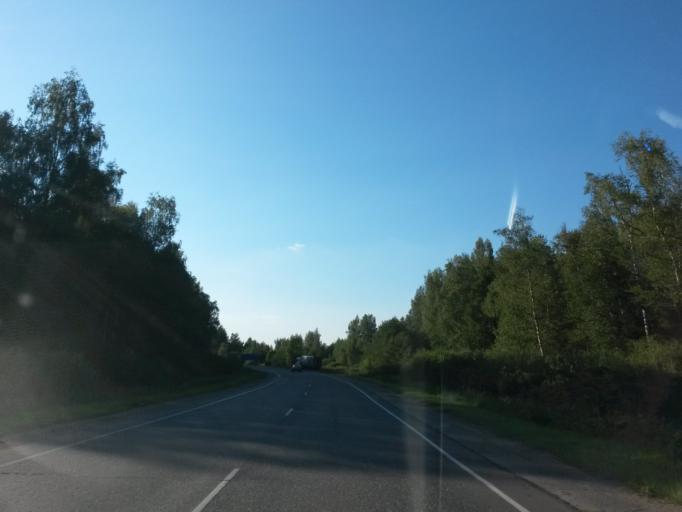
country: RU
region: Ivanovo
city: Pistsovo
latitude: 57.1163
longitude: 40.6446
